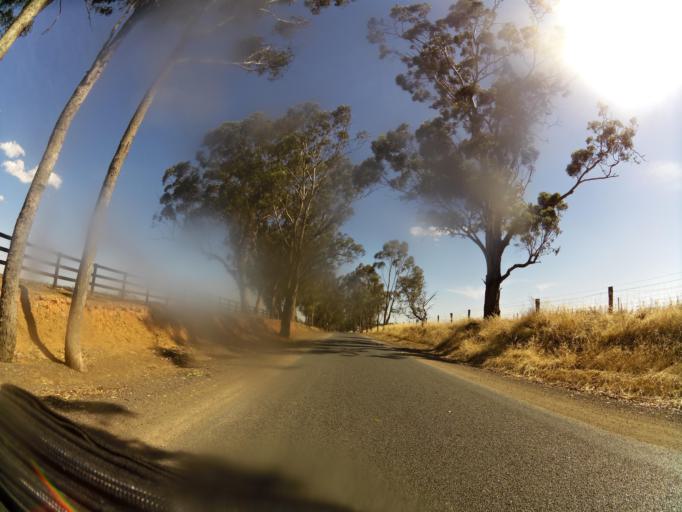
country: AU
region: Victoria
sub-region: Campaspe
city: Kyabram
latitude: -36.8603
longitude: 145.0883
